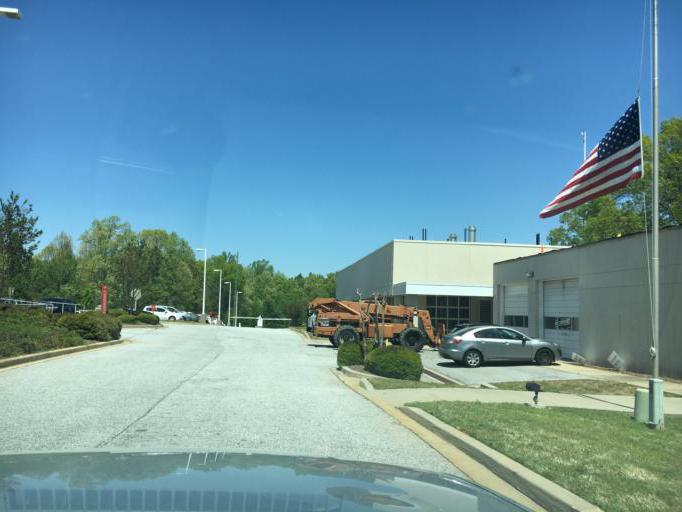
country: US
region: South Carolina
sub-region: Greenville County
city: Simpsonville
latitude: 34.7207
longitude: -82.2474
